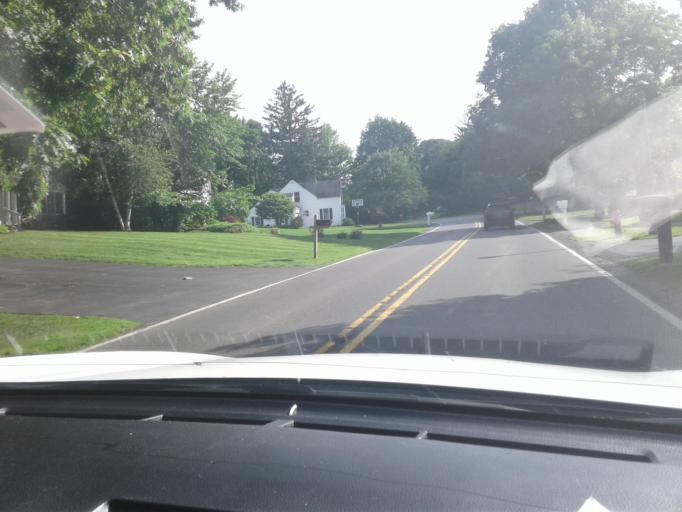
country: US
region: New York
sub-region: Onondaga County
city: East Syracuse
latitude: 43.0388
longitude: -76.0682
